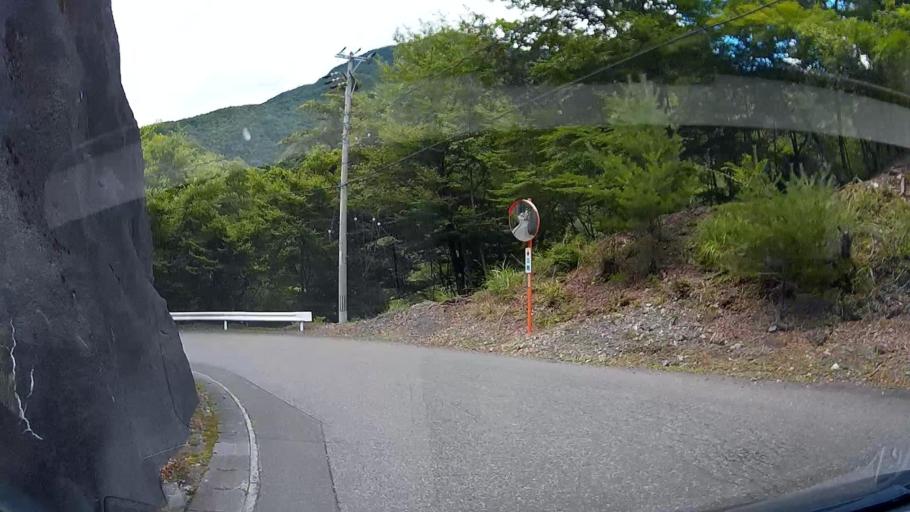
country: JP
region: Shizuoka
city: Shizuoka-shi
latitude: 35.3052
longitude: 138.2041
